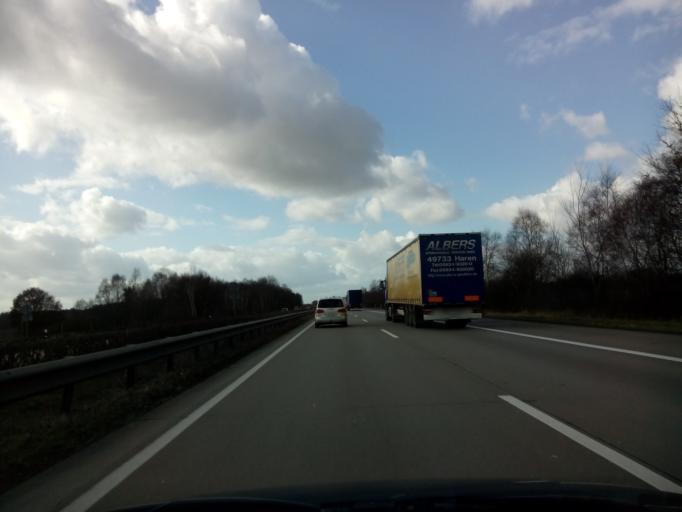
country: DE
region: Lower Saxony
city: Prinzhofte
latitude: 52.9505
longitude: 8.5421
